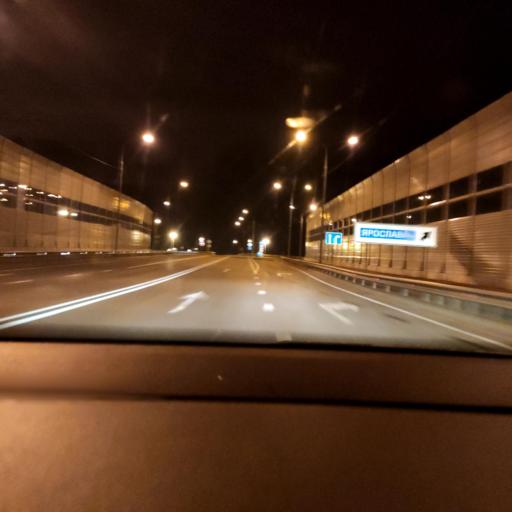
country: RU
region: Moskovskaya
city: Bolshevo
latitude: 55.9509
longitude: 37.8293
